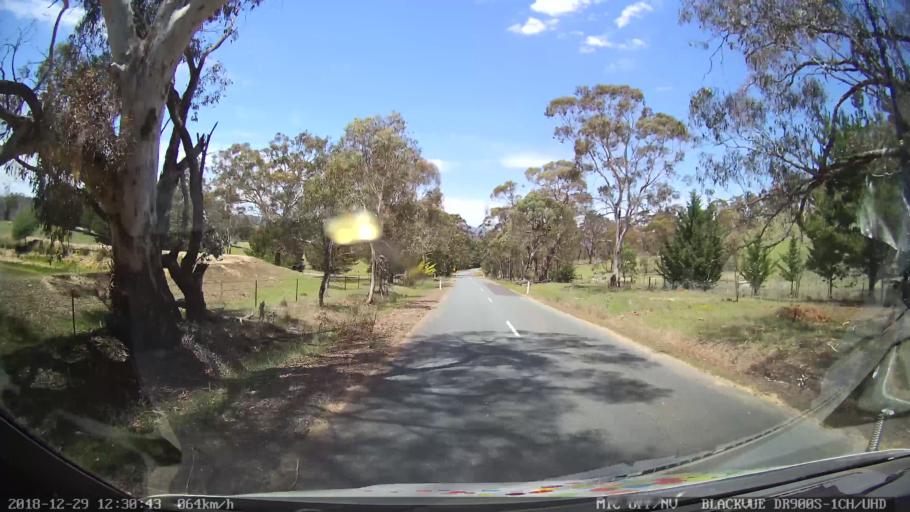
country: AU
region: Australian Capital Territory
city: Macarthur
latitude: -35.5085
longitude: 149.2329
